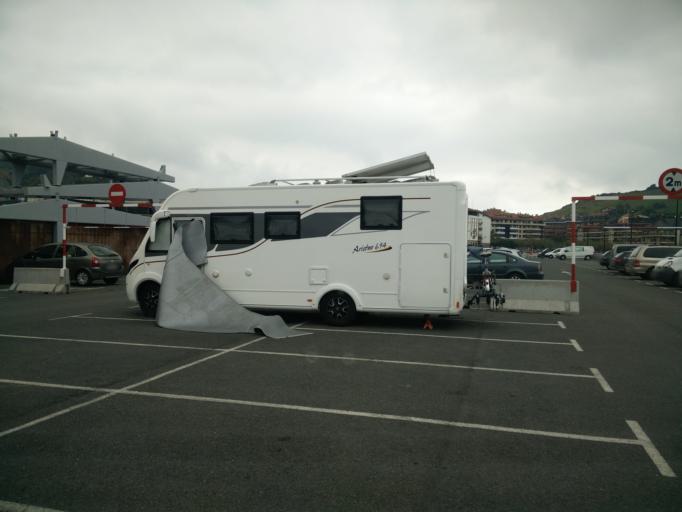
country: ES
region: Basque Country
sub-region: Provincia de Guipuzcoa
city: Zumaia
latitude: 43.2959
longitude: -2.2536
